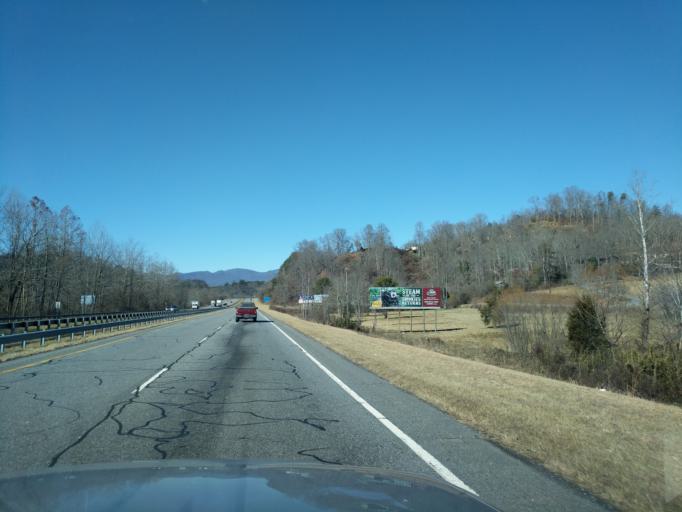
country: US
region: North Carolina
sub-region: Swain County
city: Cherokee
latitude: 35.4246
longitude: -83.3492
